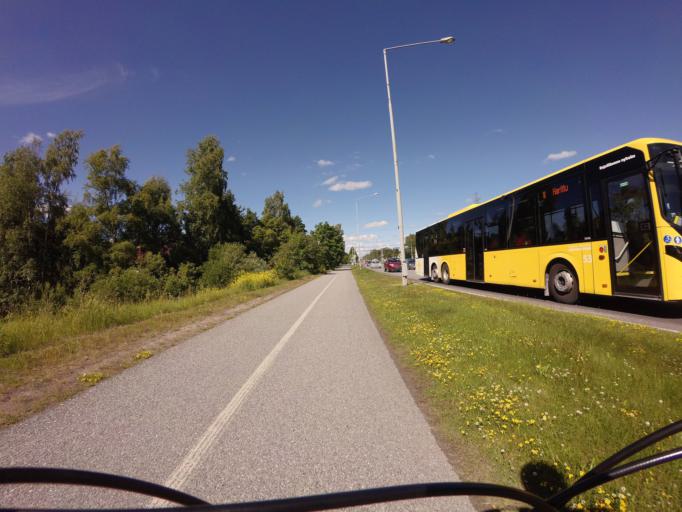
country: FI
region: Varsinais-Suomi
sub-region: Turku
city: Turku
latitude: 60.4741
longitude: 22.2648
